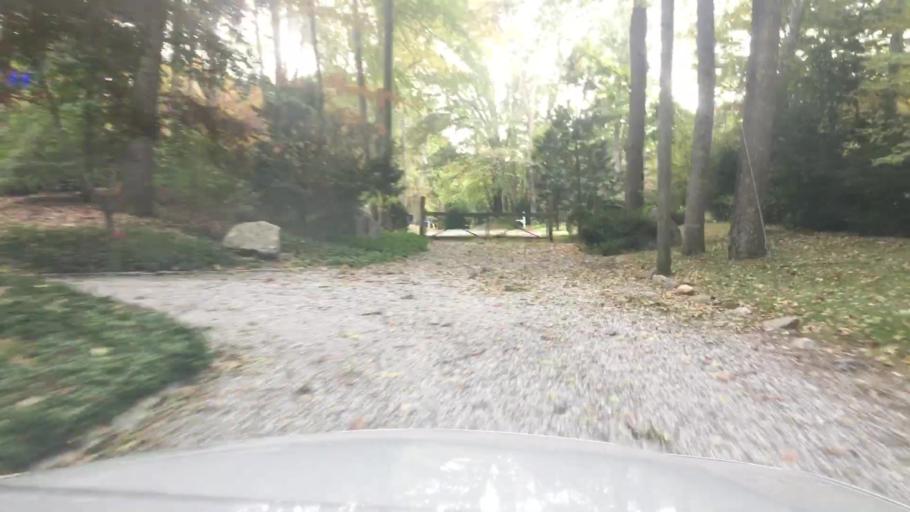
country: US
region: Connecticut
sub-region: Middlesex County
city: Essex Village
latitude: 41.3584
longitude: -72.4056
